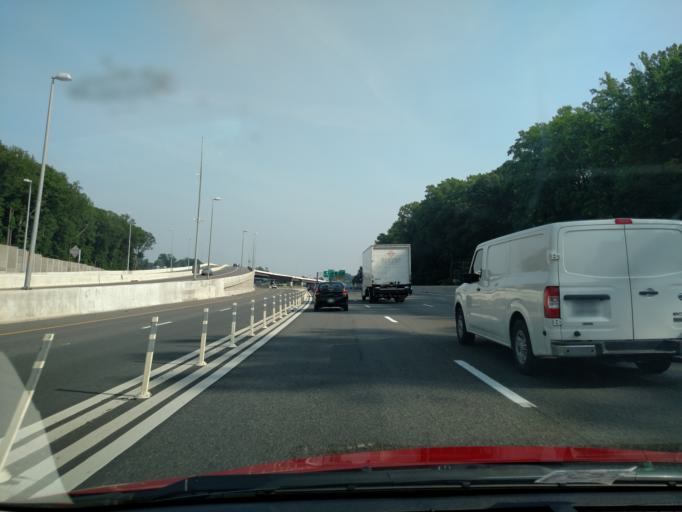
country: US
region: Virginia
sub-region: Fairfax County
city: Ravensworth
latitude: 38.8161
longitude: -77.2215
